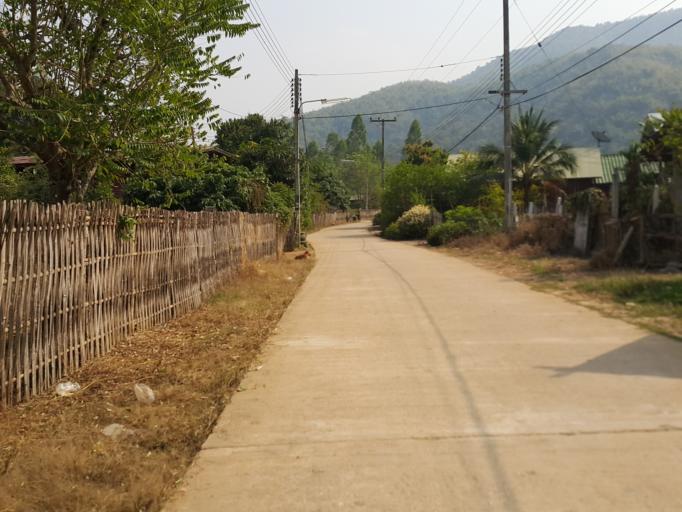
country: TH
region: Sukhothai
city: Thung Saliam
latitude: 17.3337
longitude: 99.4813
